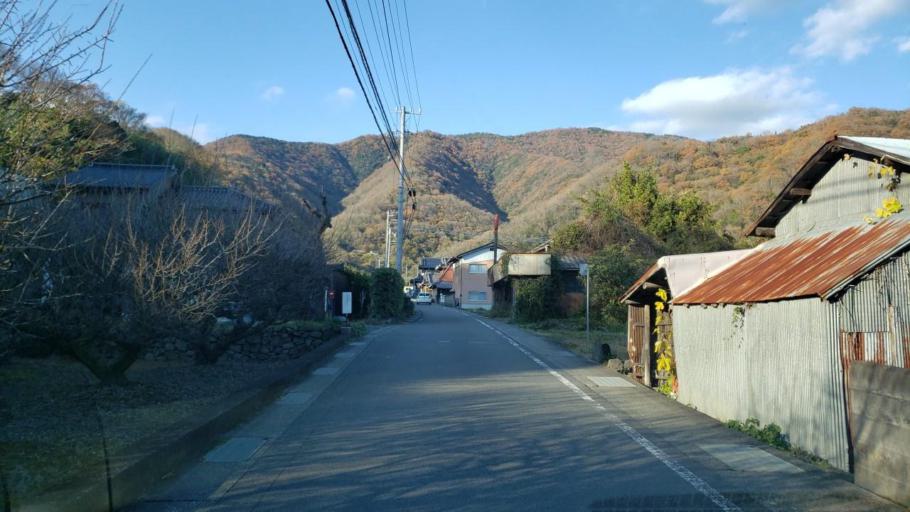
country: JP
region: Tokushima
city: Wakimachi
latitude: 34.0711
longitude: 134.0846
